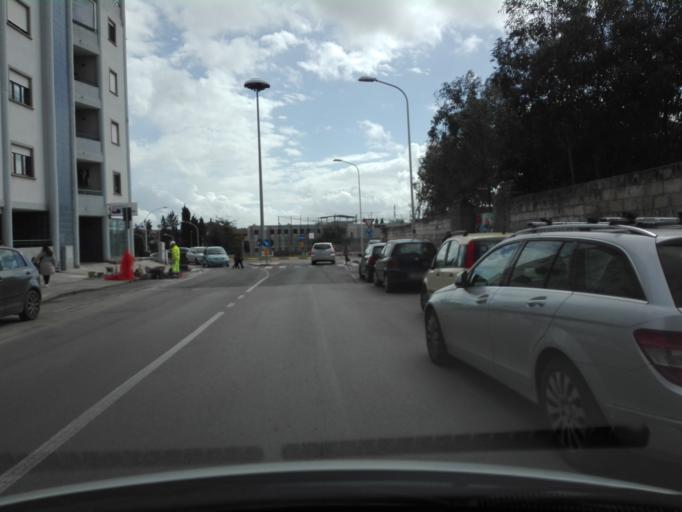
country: IT
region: Sardinia
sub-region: Provincia di Sassari
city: Sassari
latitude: 40.7249
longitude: 8.5759
